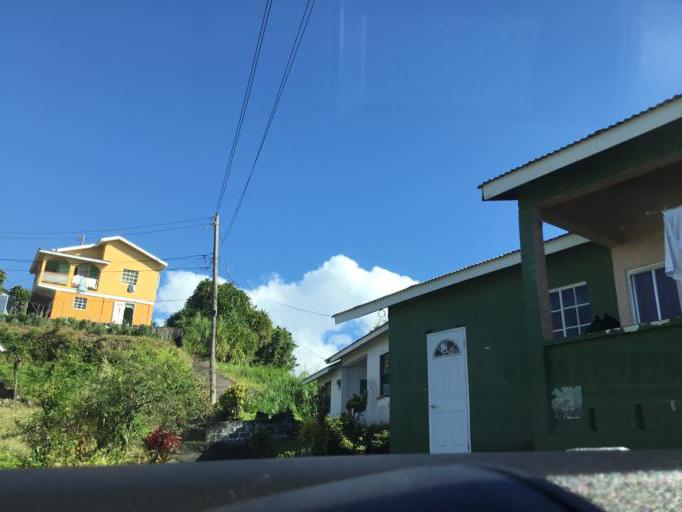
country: VC
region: Saint David
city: Chateaubelair
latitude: 13.2703
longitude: -61.2420
